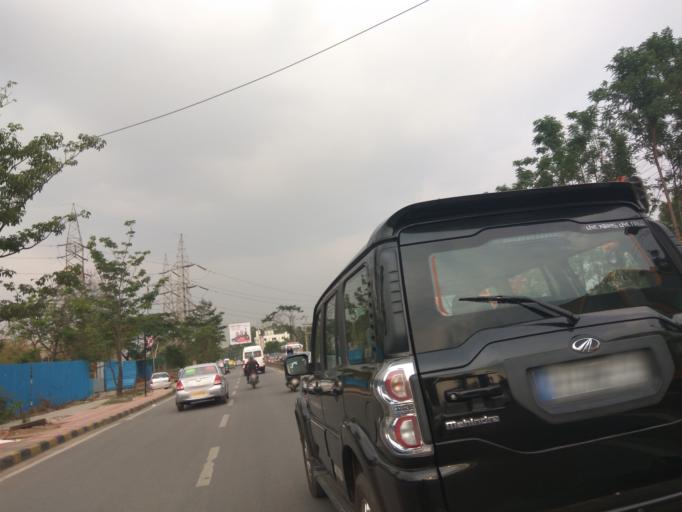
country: IN
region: Karnataka
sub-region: Bangalore Urban
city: Bangalore
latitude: 12.9776
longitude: 77.7153
